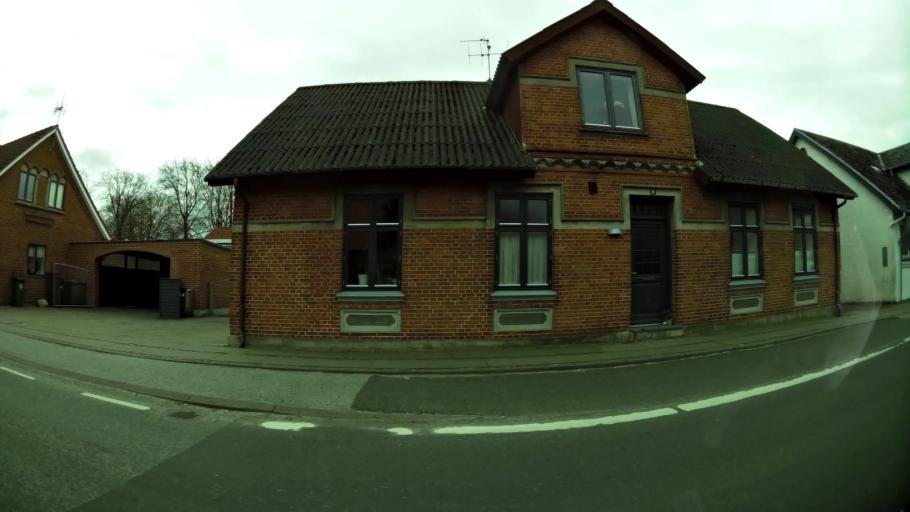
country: DK
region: North Denmark
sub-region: Jammerbugt Kommune
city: Fjerritslev
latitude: 57.0881
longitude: 9.2696
